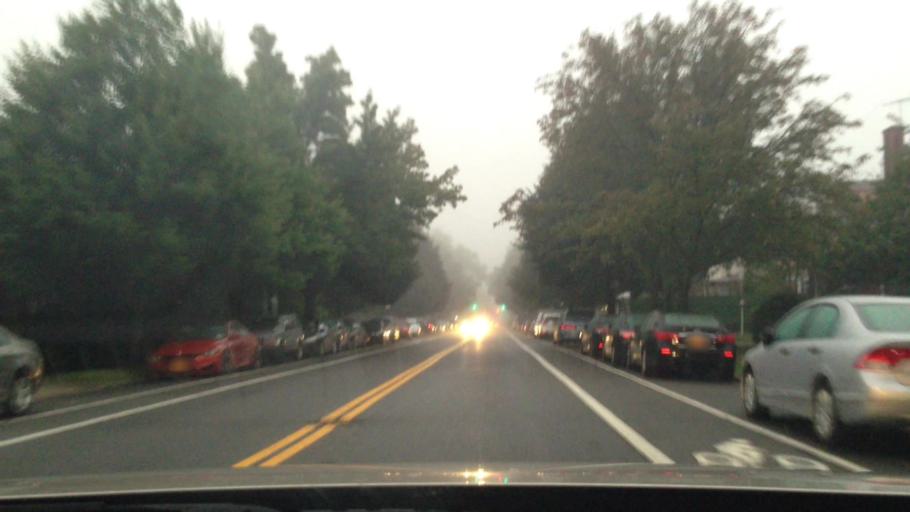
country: US
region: New York
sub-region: Kings County
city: Brooklyn
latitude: 40.6161
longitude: -73.9497
